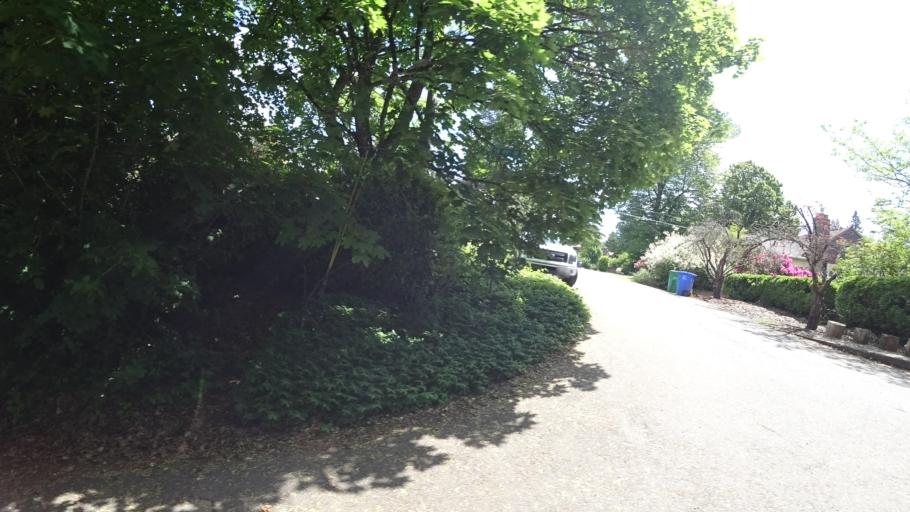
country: US
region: Oregon
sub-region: Washington County
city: Garden Home-Whitford
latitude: 45.4614
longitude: -122.7232
